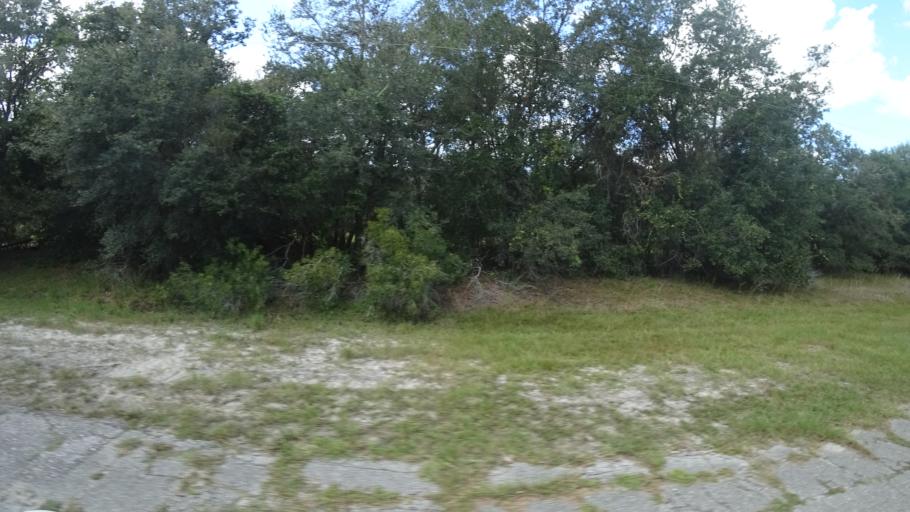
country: US
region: Florida
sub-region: Sarasota County
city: Lake Sarasota
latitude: 27.2754
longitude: -82.2281
